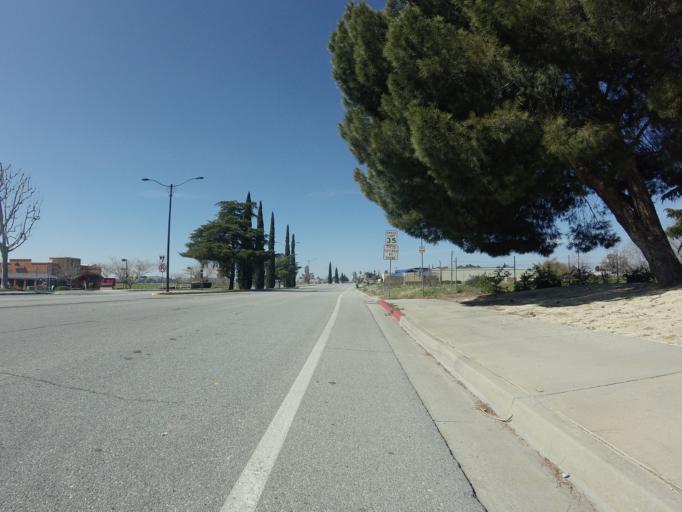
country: US
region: California
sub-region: Riverside County
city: Beaumont
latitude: 33.9295
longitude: -116.9498
